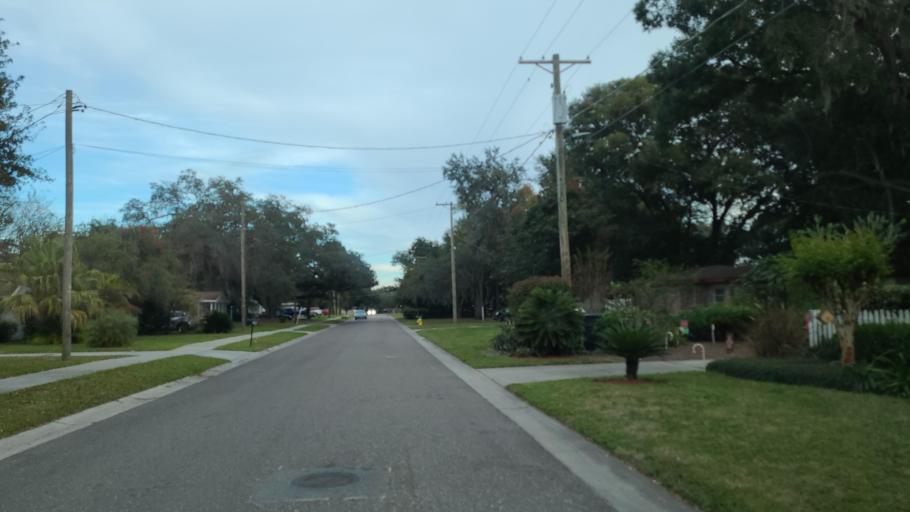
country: US
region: Florida
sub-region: Hillsborough County
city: Brandon
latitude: 27.9419
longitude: -82.2849
